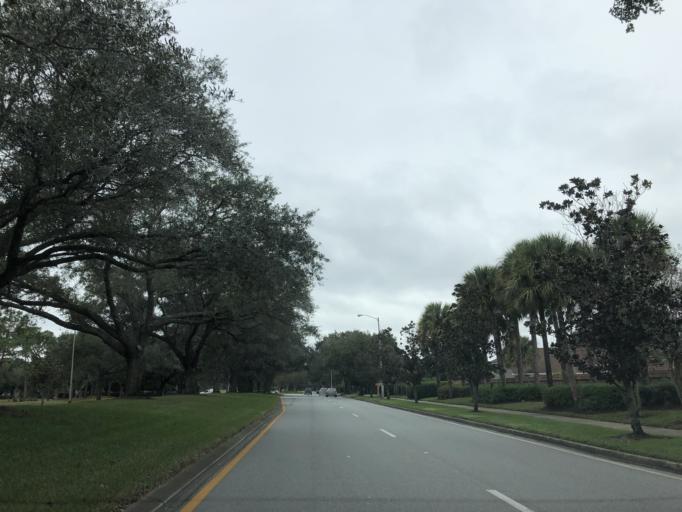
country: US
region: Florida
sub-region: Orange County
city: Hunters Creek
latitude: 28.3679
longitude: -81.4097
